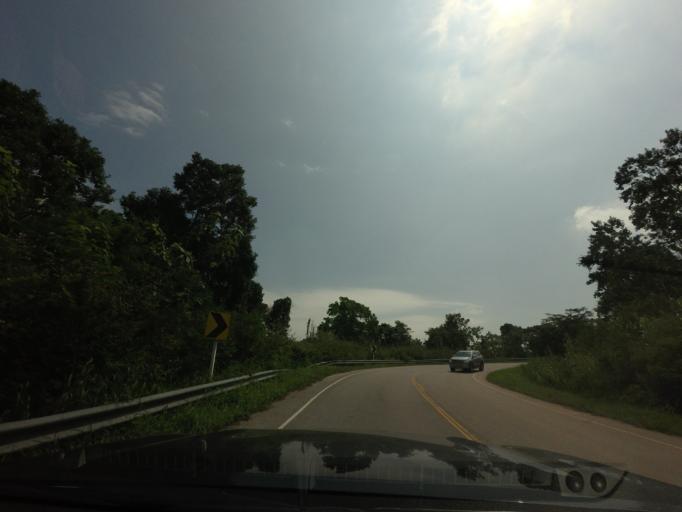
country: TH
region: Loei
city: Phu Ruea
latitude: 17.5056
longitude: 101.4651
